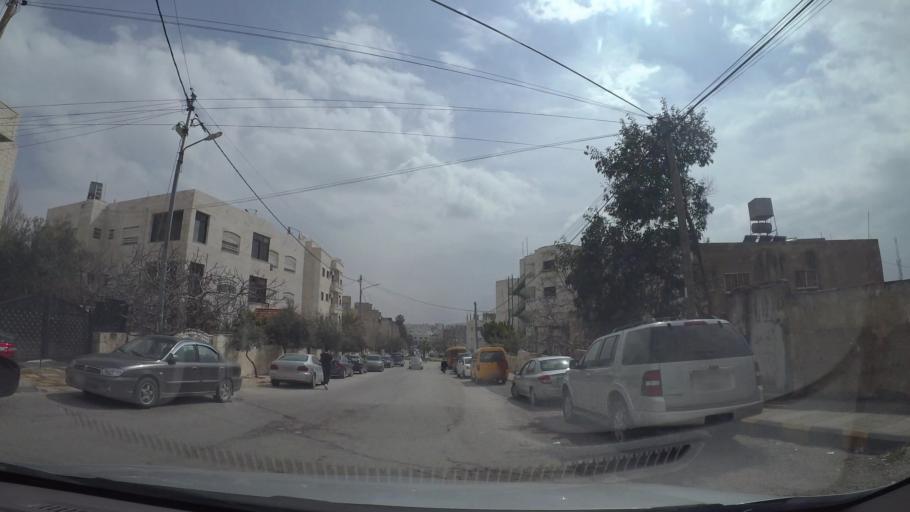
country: JO
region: Amman
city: Umm as Summaq
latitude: 31.8998
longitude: 35.8392
